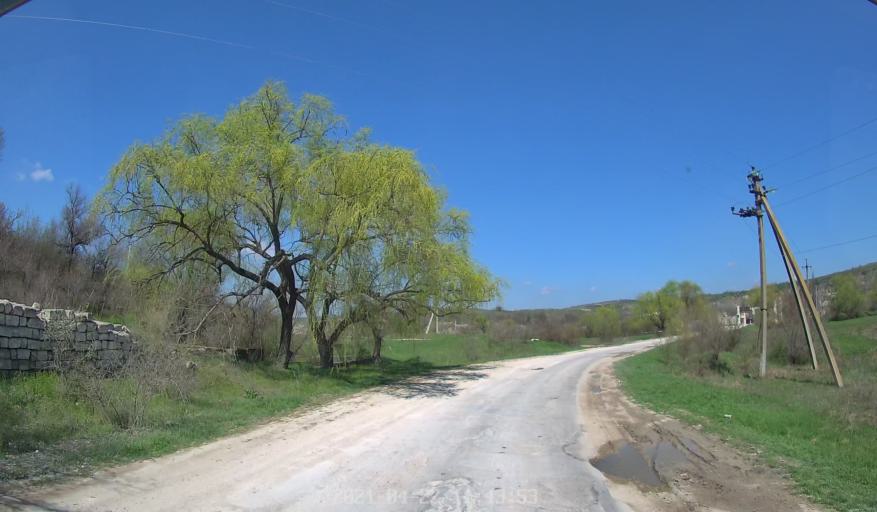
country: MD
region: Chisinau
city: Ciorescu
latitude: 47.1404
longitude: 28.8972
